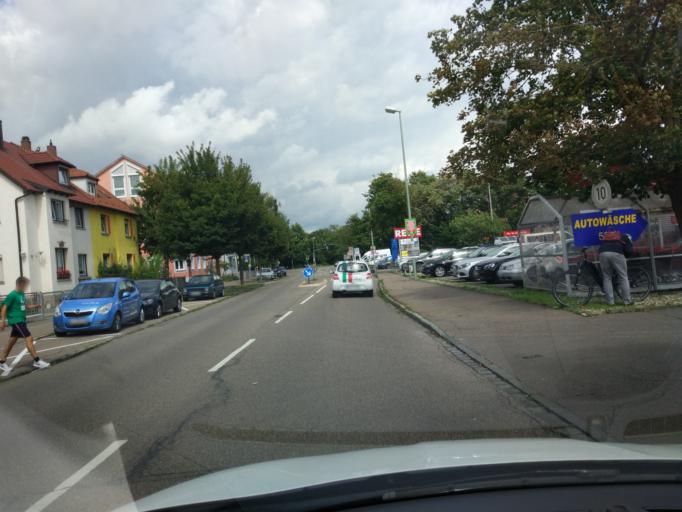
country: DE
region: Bavaria
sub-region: Swabia
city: Neu-Ulm
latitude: 48.4063
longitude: 10.0056
